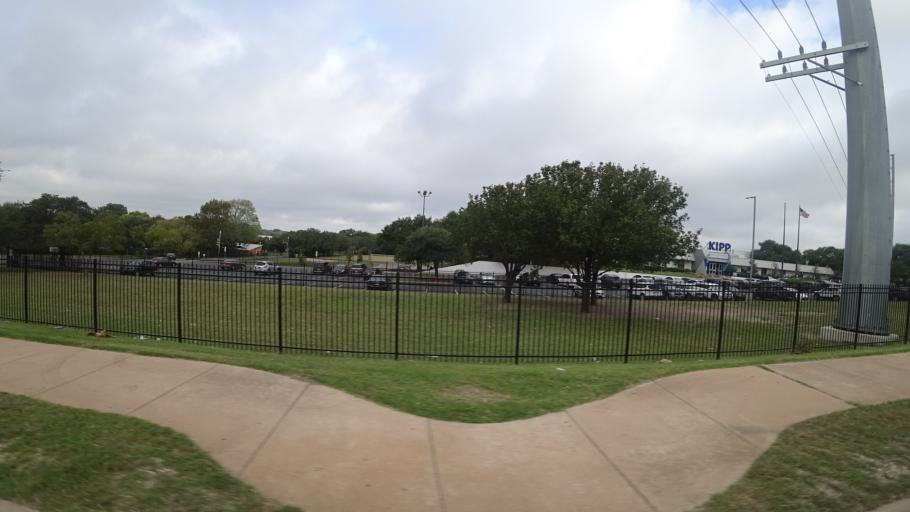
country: US
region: Texas
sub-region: Travis County
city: Austin
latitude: 30.3347
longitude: -97.6851
